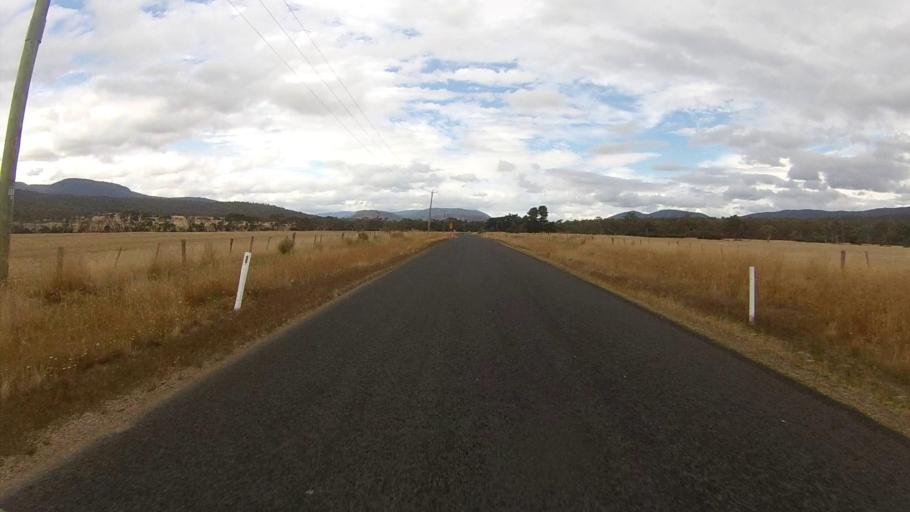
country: AU
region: Tasmania
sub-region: Break O'Day
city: St Helens
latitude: -41.8220
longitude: 147.8802
